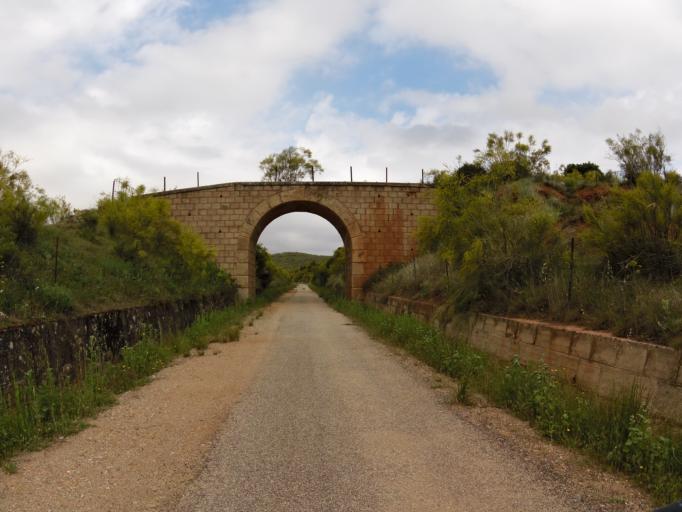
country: ES
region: Castille-La Mancha
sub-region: Provincia de Albacete
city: Alcaraz
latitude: 38.7028
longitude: -2.4892
